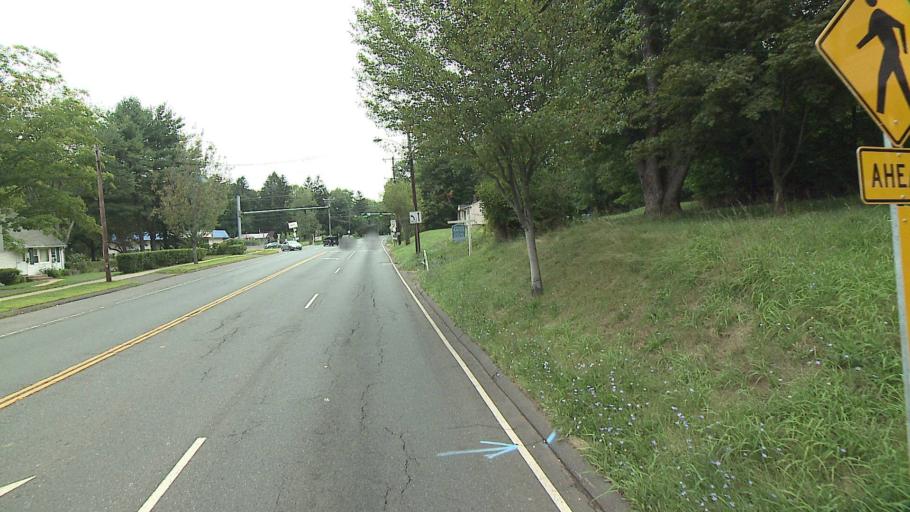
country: US
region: Connecticut
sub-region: Middlesex County
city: Middletown
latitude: 41.5644
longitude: -72.6695
